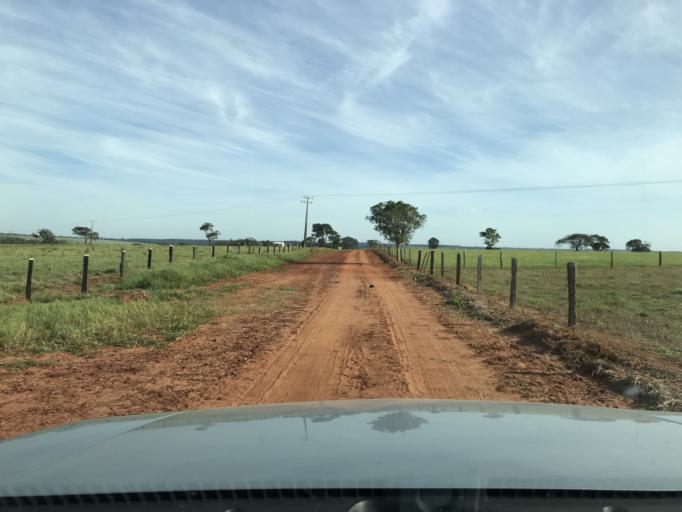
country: BR
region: Mato Grosso do Sul
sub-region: Iguatemi
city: Iguatemi
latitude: -23.6564
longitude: -54.5713
